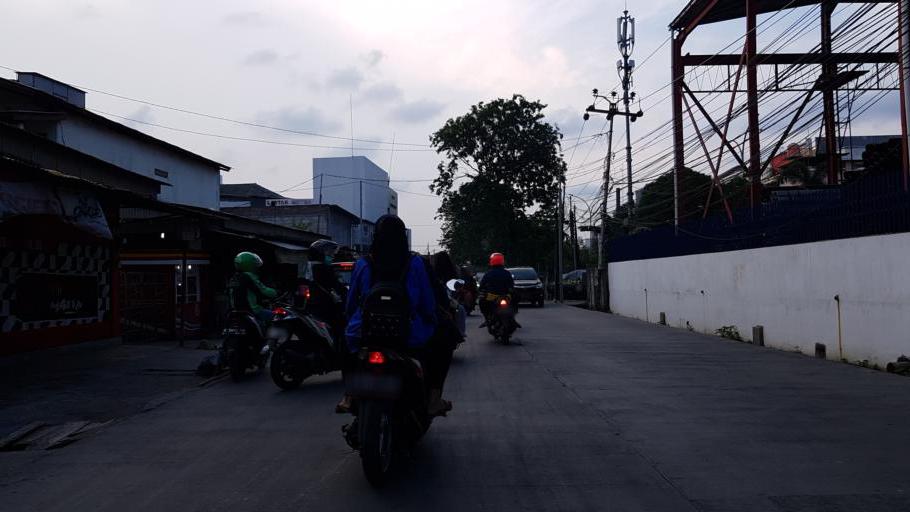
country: ID
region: West Java
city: Ciputat
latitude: -6.1367
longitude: 106.7564
